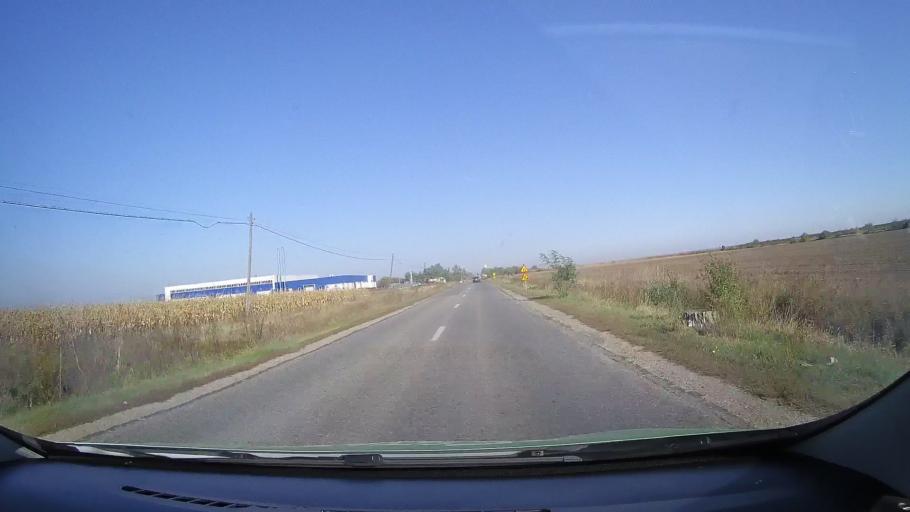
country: RO
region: Satu Mare
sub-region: Oras Tasnad
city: Tasnad
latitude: 47.5039
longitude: 22.5740
